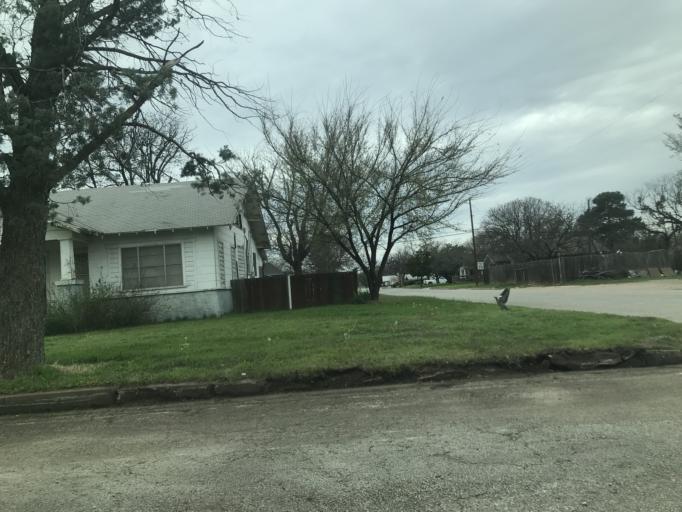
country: US
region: Texas
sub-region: Taylor County
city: Abilene
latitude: 32.4586
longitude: -99.7454
